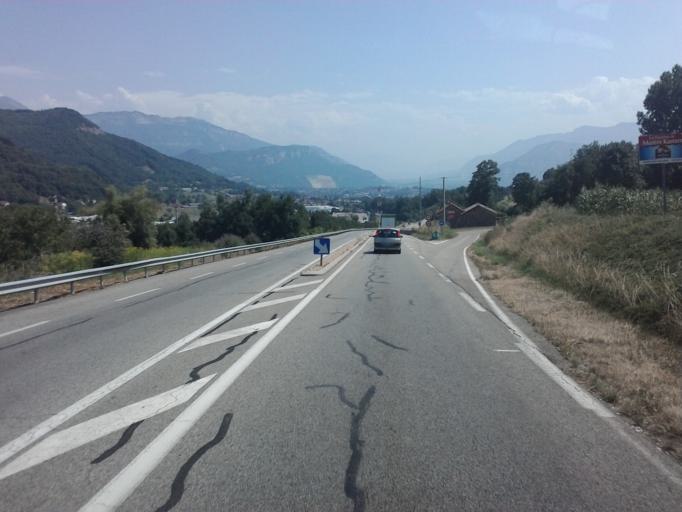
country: FR
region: Rhone-Alpes
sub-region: Departement de l'Isere
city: Chirens
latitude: 45.3908
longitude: 5.5721
